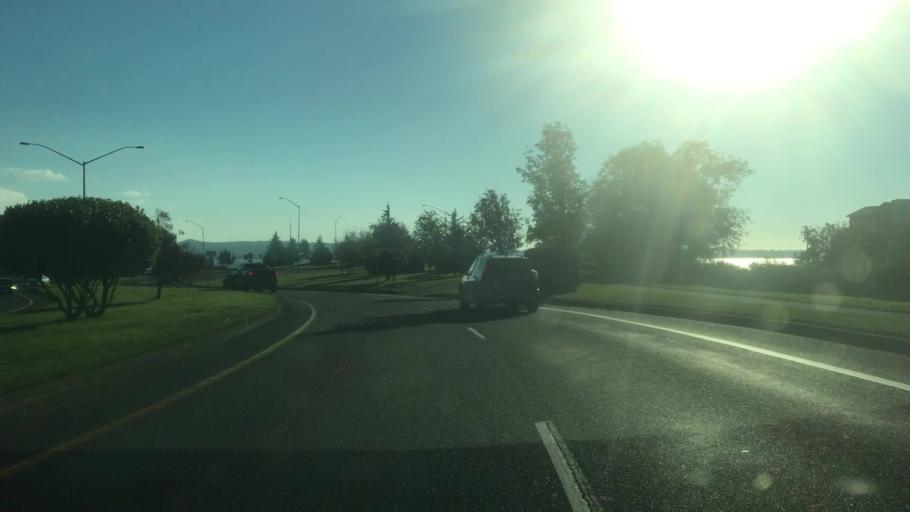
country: US
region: Oregon
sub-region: Clatsop County
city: Astoria
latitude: 46.1845
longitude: -123.8595
